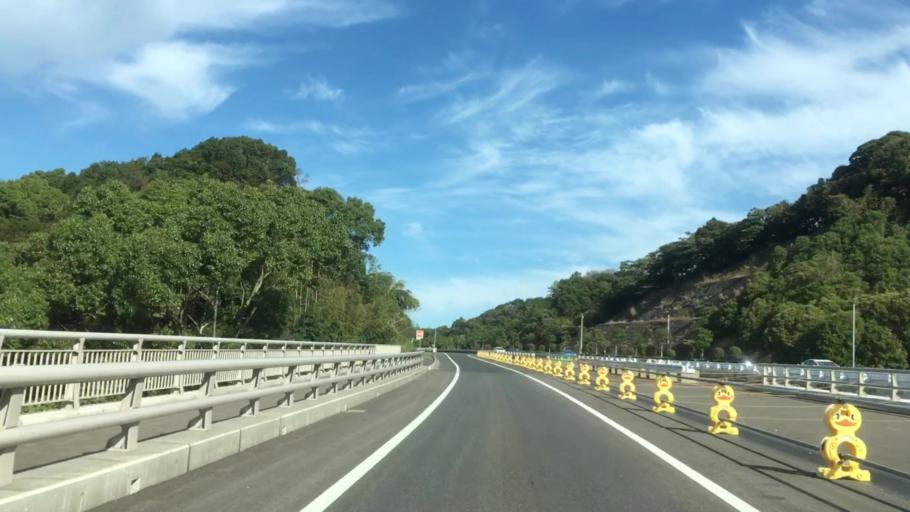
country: JP
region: Nagasaki
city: Sasebo
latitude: 33.1198
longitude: 129.7924
